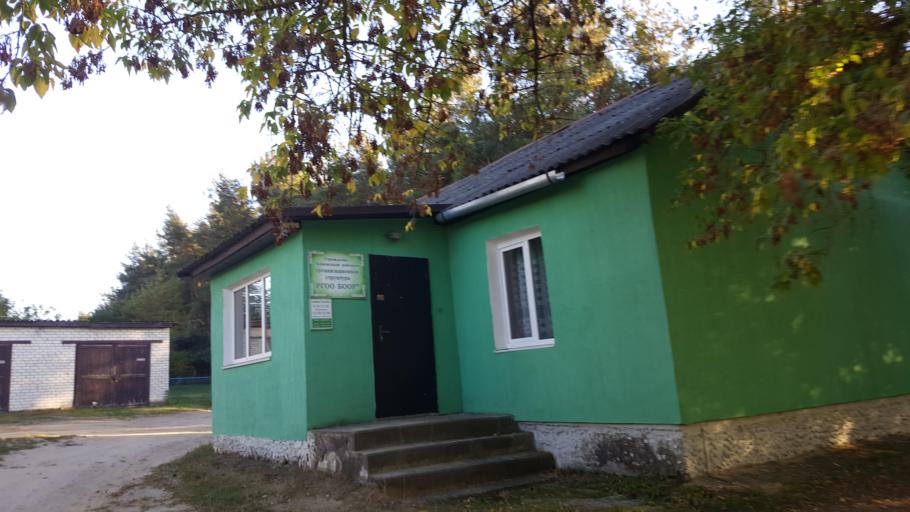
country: BY
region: Brest
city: Kamyanyets
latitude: 52.3945
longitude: 23.8354
